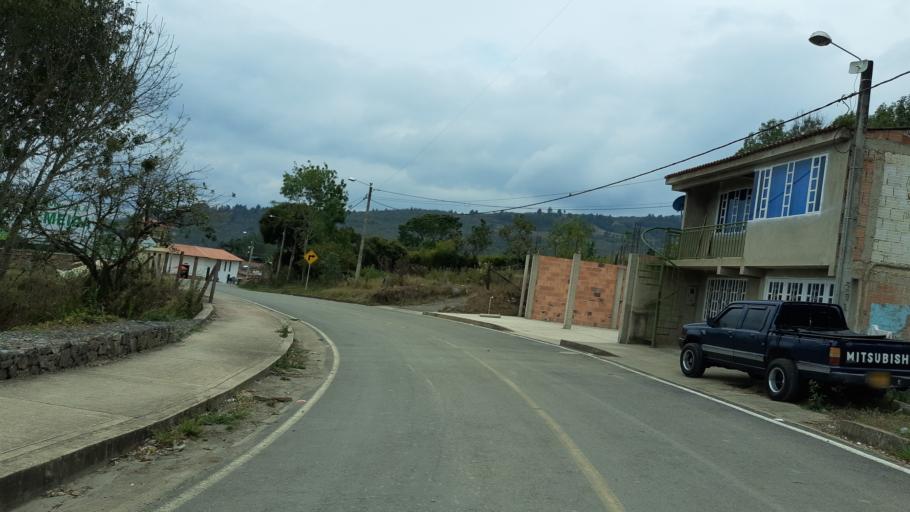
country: CO
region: Boyaca
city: Somondoco
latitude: 4.9703
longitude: -73.3803
